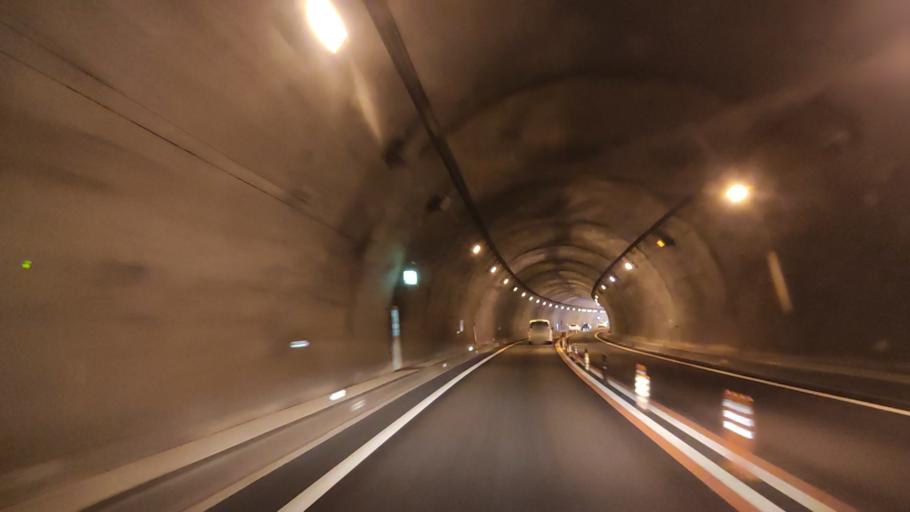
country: JP
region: Ehime
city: Kawanoecho
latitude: 33.9962
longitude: 133.6355
